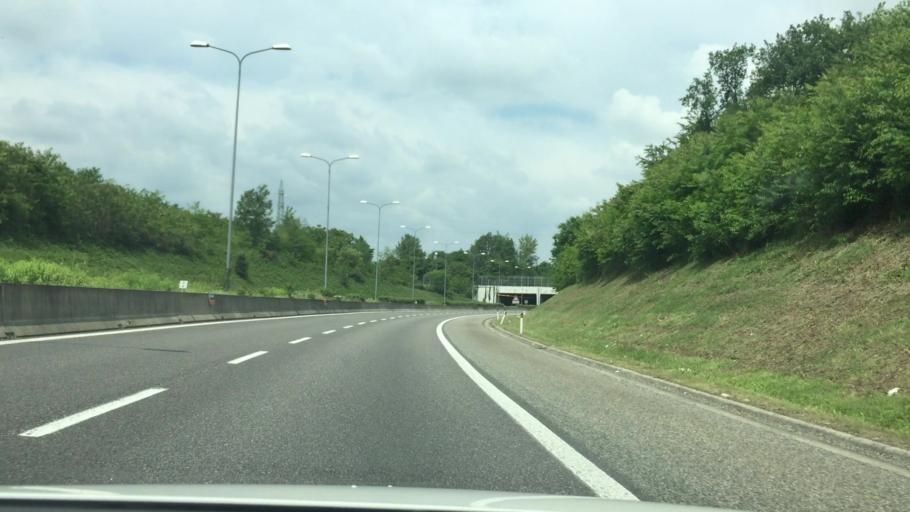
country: IT
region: Lombardy
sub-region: Provincia di Varese
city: Lonate Pozzolo
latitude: 45.5885
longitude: 8.7162
